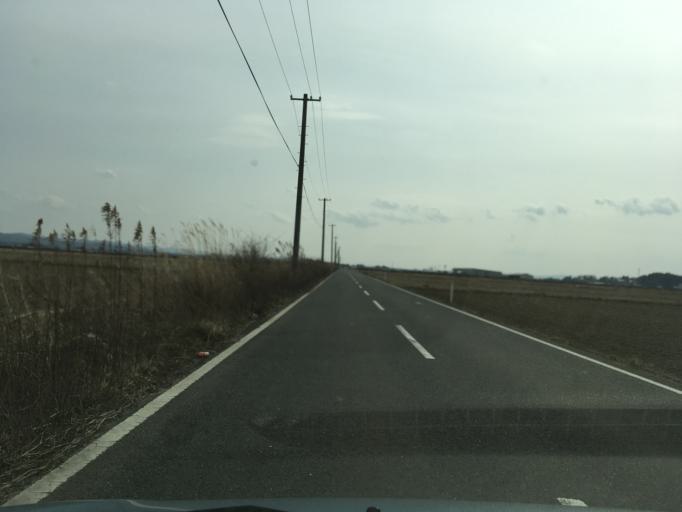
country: JP
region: Iwate
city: Ichinoseki
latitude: 38.7433
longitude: 141.2378
